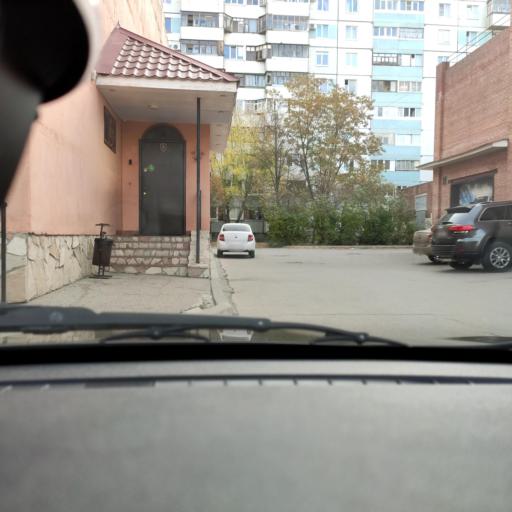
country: RU
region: Samara
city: Tol'yatti
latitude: 53.5462
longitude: 49.3475
